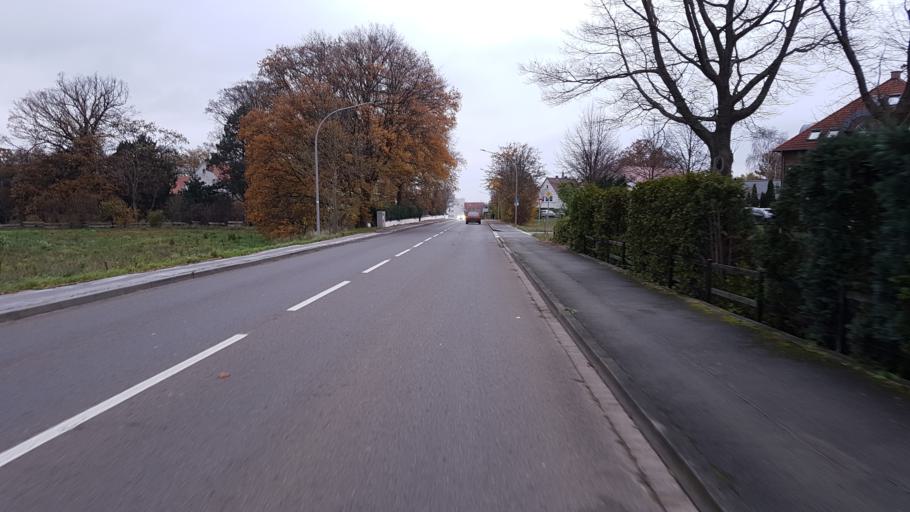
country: DE
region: North Rhine-Westphalia
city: Rahden
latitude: 52.4294
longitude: 8.6066
